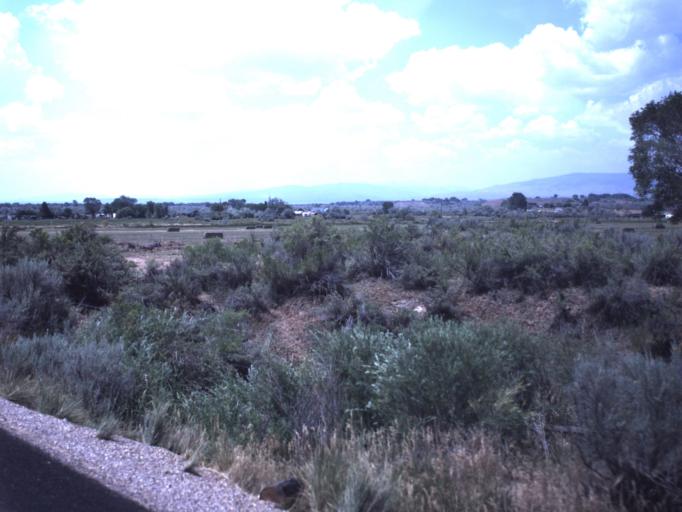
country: US
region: Utah
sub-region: Duchesne County
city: Roosevelt
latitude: 40.4037
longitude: -109.8513
